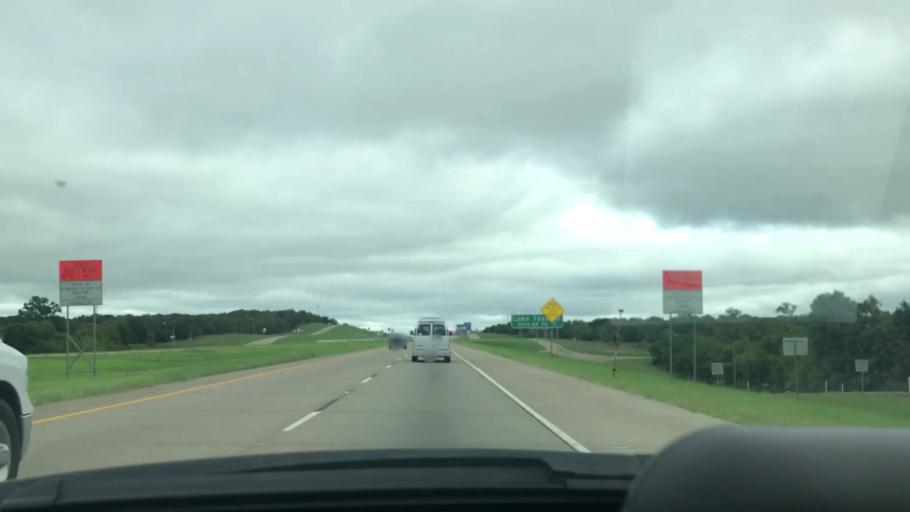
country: US
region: Texas
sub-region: Grayson County
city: Denison
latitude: 33.7453
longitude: -96.5855
